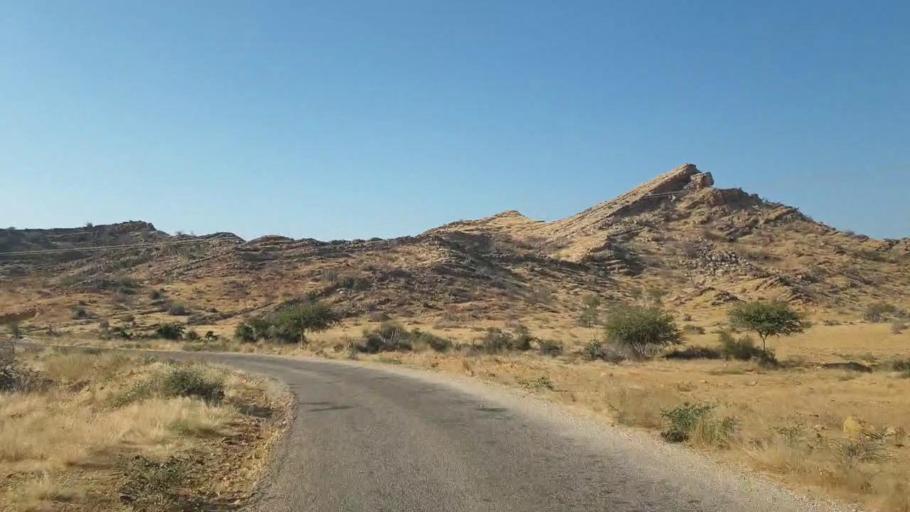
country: PK
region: Sindh
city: Malir Cantonment
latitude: 25.4048
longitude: 67.4845
